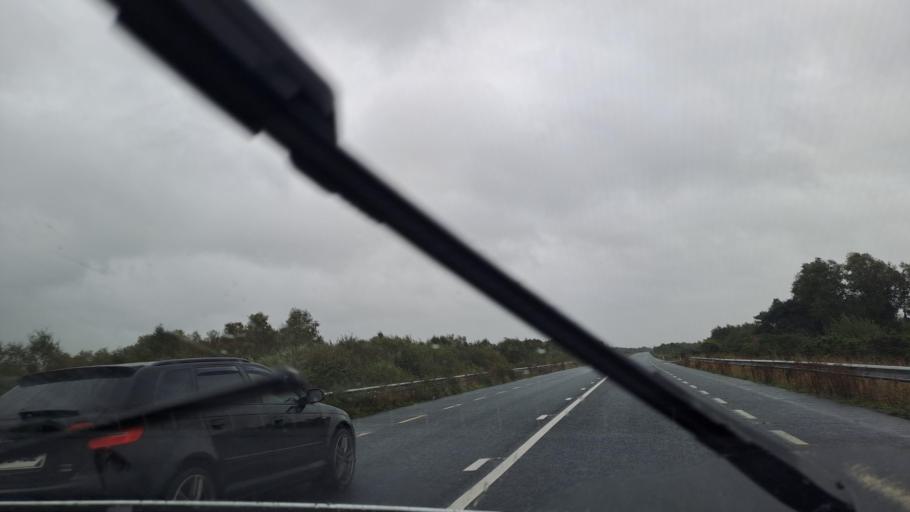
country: IE
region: Ulster
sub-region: County Monaghan
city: Carrickmacross
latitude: 53.9735
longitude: -6.6249
